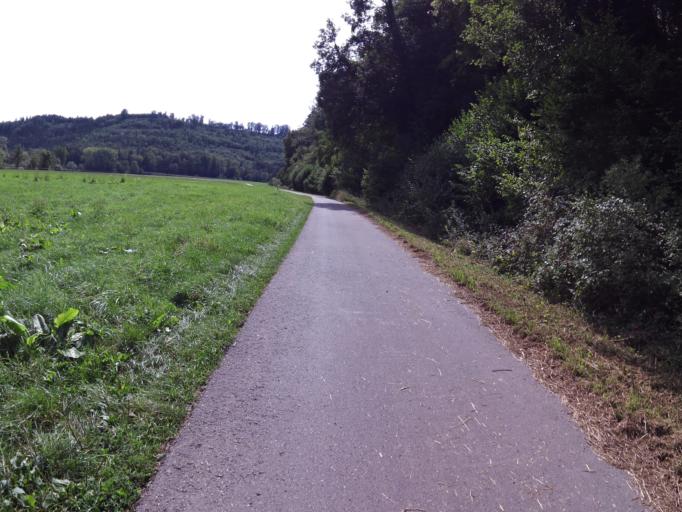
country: DE
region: Baden-Wuerttemberg
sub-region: Freiburg Region
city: Sulz am Neckar
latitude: 48.4005
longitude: 8.6406
